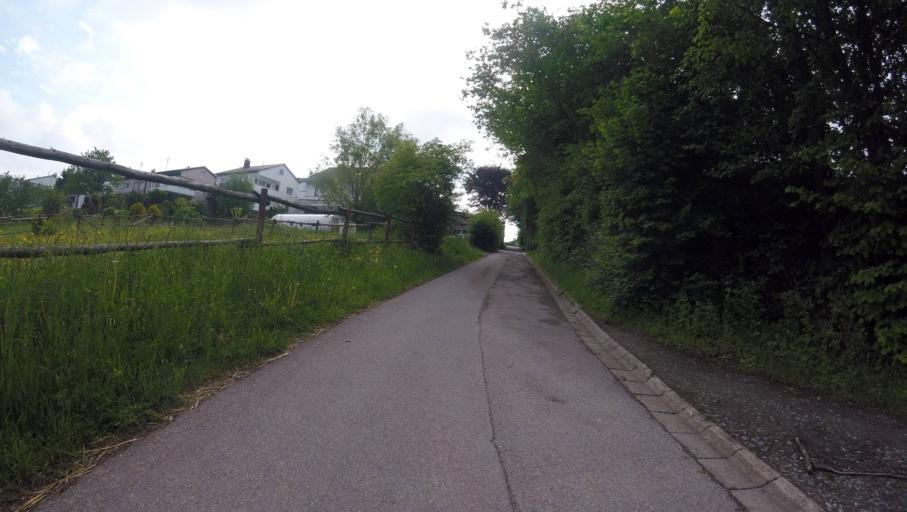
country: DE
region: Baden-Wuerttemberg
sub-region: Regierungsbezirk Stuttgart
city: Rudersberg
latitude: 48.9371
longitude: 9.5167
